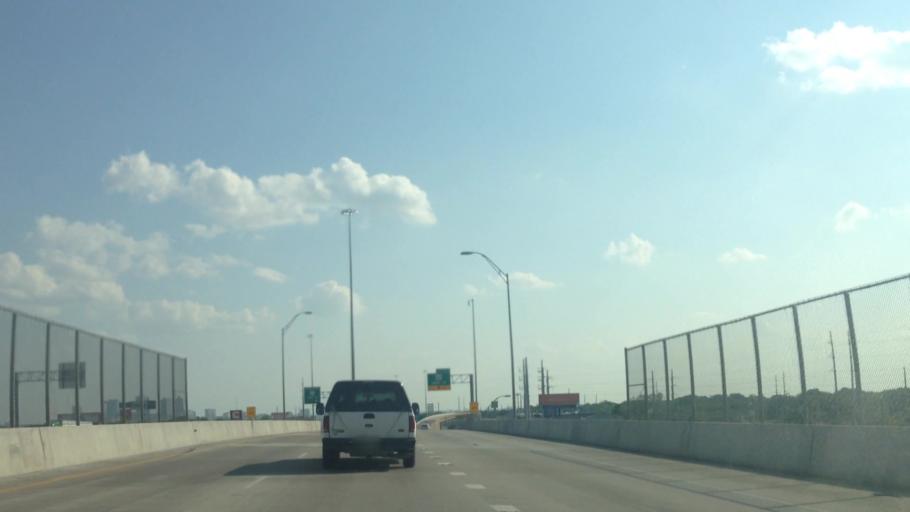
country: US
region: Texas
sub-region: Tarrant County
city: Haltom City
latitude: 32.8068
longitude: -97.3163
